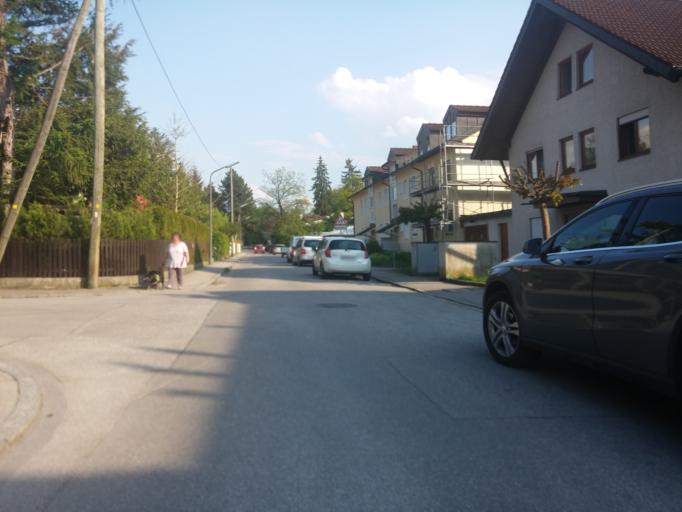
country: DE
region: Bavaria
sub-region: Upper Bavaria
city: Haar
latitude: 48.1122
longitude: 11.6962
